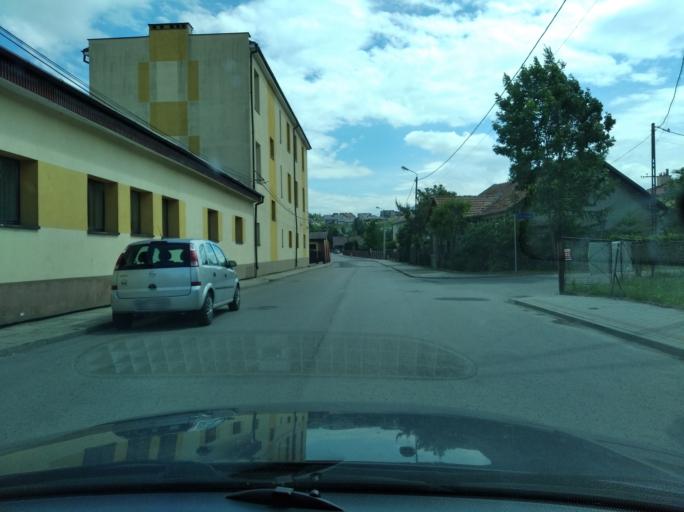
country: PL
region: Subcarpathian Voivodeship
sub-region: Powiat ropczycko-sedziszowski
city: Ropczyce
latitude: 50.0531
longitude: 21.6148
